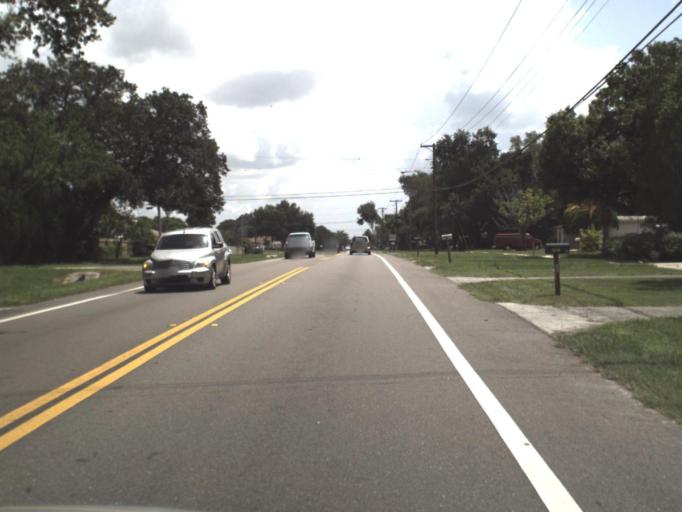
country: US
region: Florida
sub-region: Pinellas County
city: Safety Harbor
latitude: 27.9826
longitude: -82.7245
